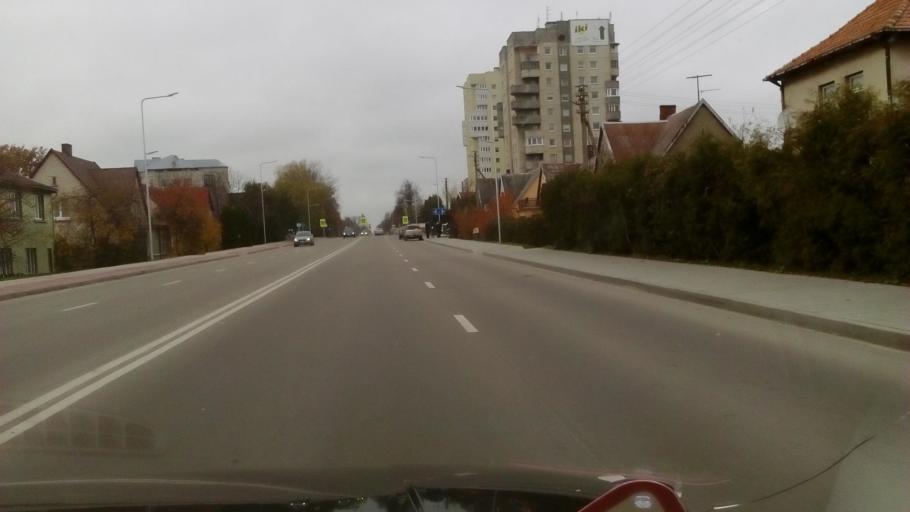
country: LT
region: Marijampoles apskritis
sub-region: Marijampole Municipality
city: Marijampole
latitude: 54.5616
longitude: 23.3373
